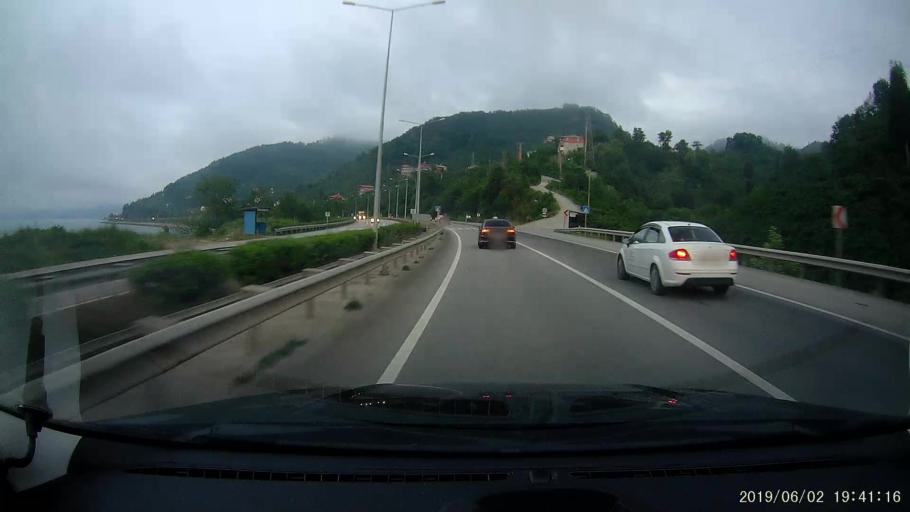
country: TR
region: Giresun
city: Kesap
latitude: 40.9147
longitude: 38.4766
